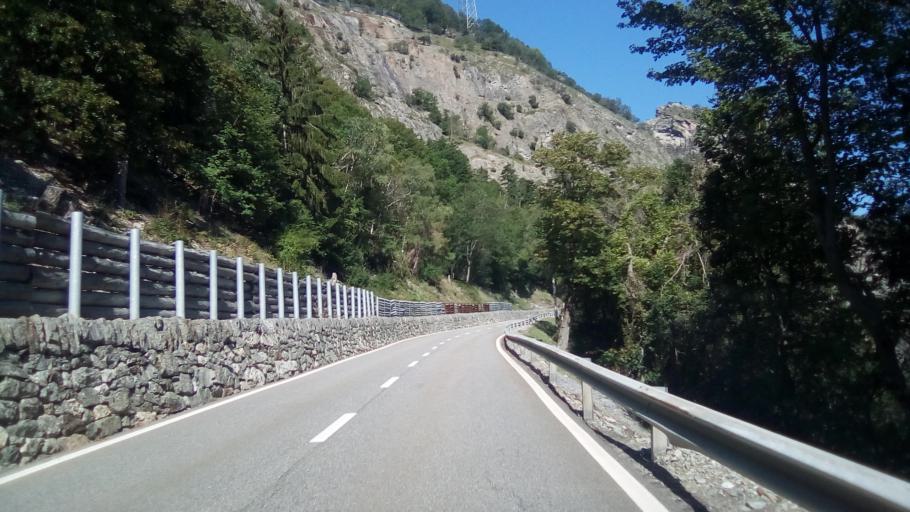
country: CH
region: Valais
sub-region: Saint-Maurice District
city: Vernayaz
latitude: 46.1190
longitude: 7.0444
